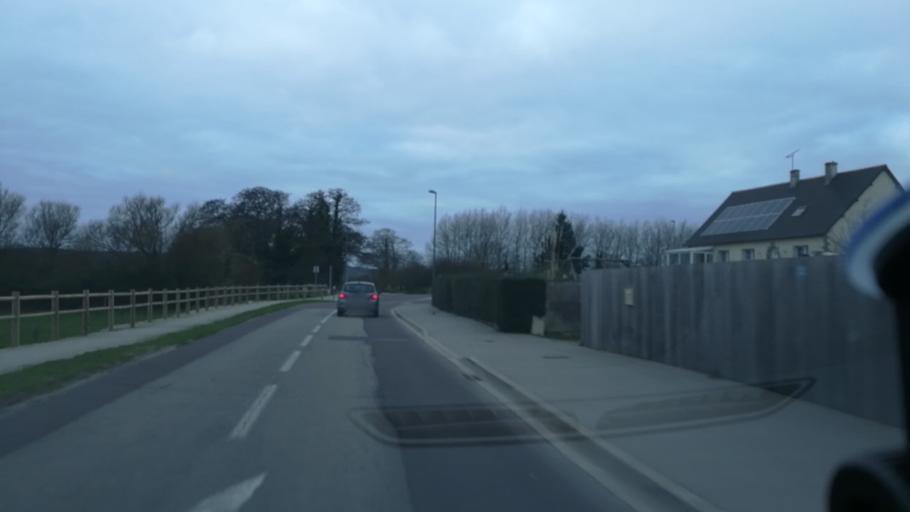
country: FR
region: Lower Normandy
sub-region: Departement de la Manche
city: Reville
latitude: 49.6151
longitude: -1.2597
